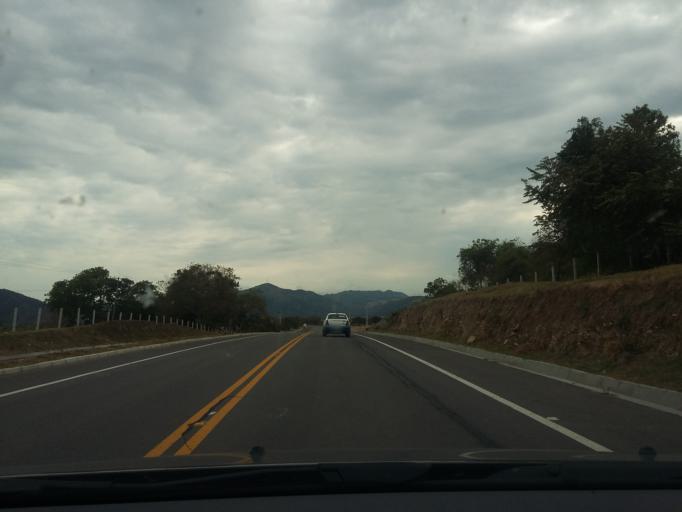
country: CO
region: Cundinamarca
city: Narino
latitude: 4.3647
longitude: -74.8440
